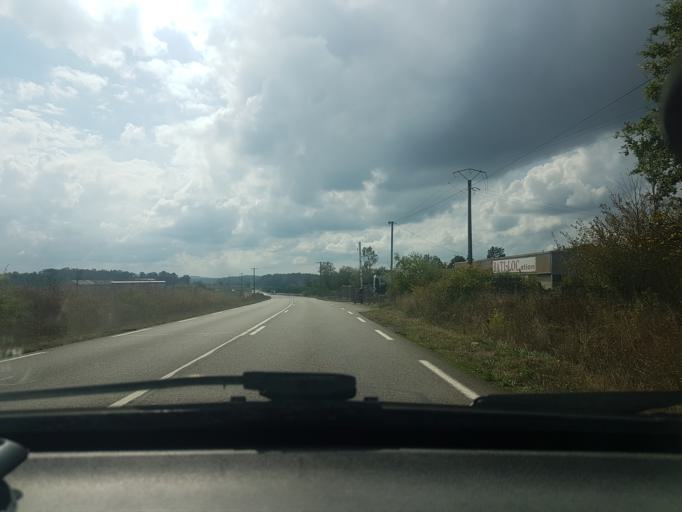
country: FR
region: Franche-Comte
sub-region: Departement de la Haute-Saone
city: Villersexel
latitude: 47.5464
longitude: 6.4355
